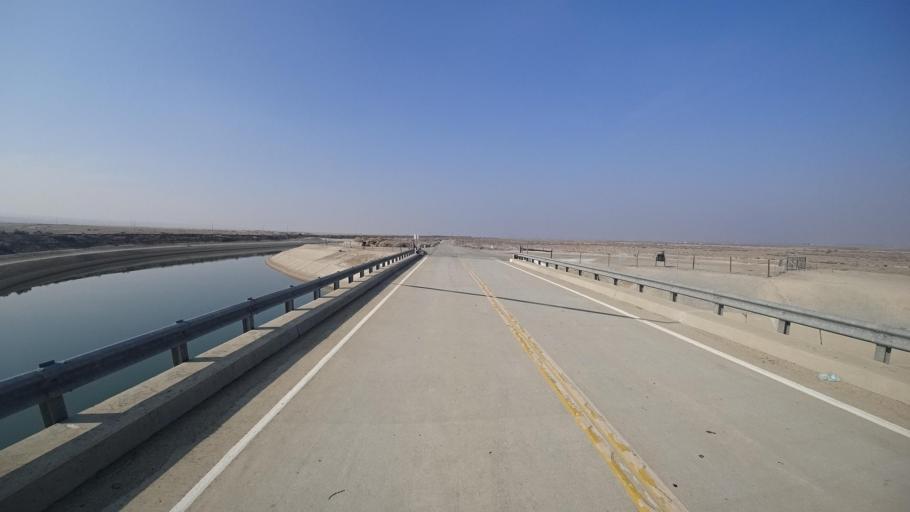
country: US
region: California
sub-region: Kern County
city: Buttonwillow
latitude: 35.3060
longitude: -119.3696
